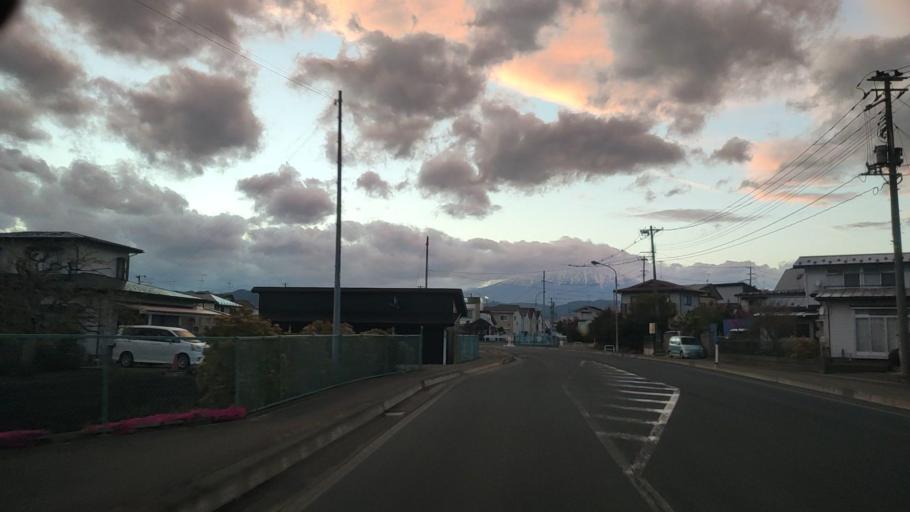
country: JP
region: Iwate
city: Morioka-shi
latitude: 39.7183
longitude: 141.1091
